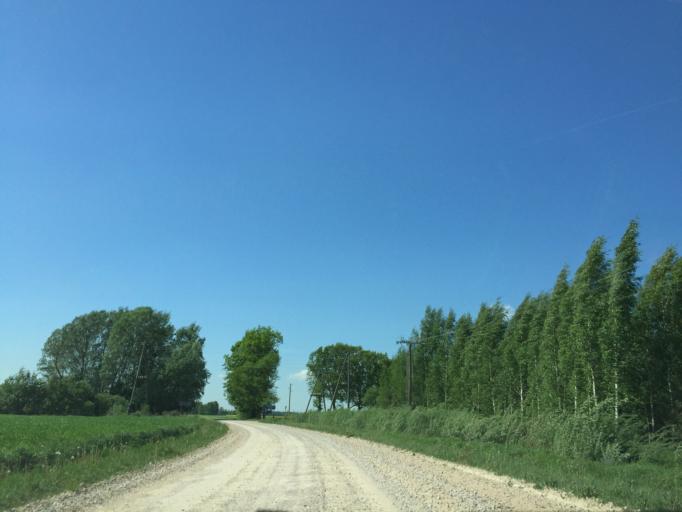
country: LV
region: Rundales
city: Pilsrundale
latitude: 56.5059
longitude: 24.0480
